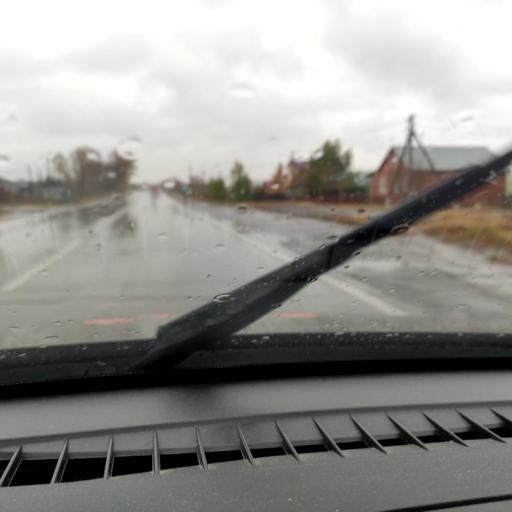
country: RU
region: Samara
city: Tol'yatti
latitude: 53.6448
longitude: 49.2948
